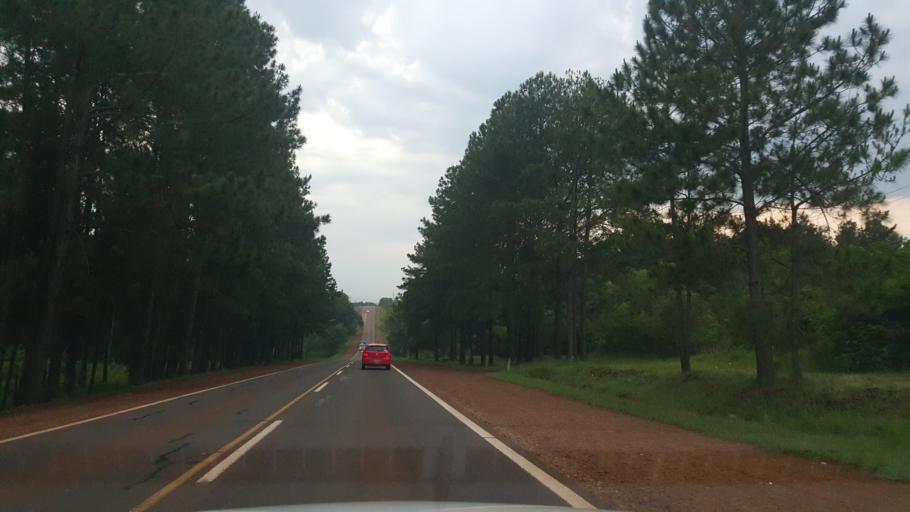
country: AR
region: Misiones
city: Santo Pipo
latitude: -27.1345
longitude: -55.3955
